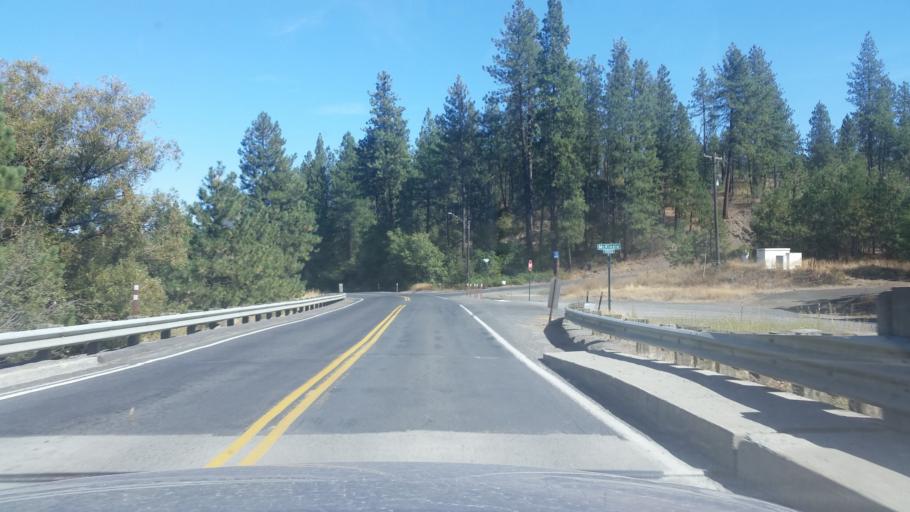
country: US
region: Washington
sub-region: Spokane County
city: Spokane
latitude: 47.5668
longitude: -117.4922
